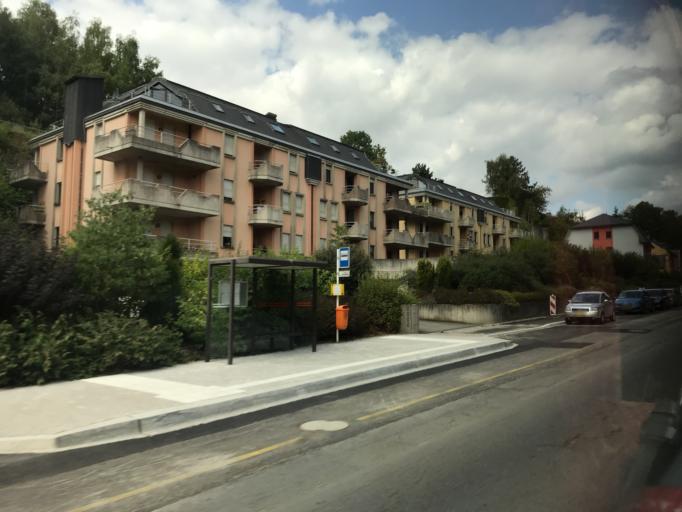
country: LU
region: Luxembourg
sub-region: Canton de Luxembourg
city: Hesperange
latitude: 49.5812
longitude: 6.1490
